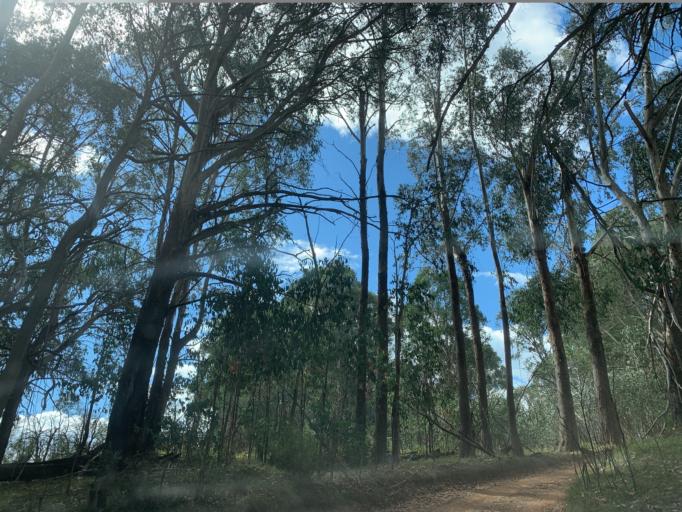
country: AU
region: Victoria
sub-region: Mansfield
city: Mansfield
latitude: -37.1043
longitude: 146.5357
